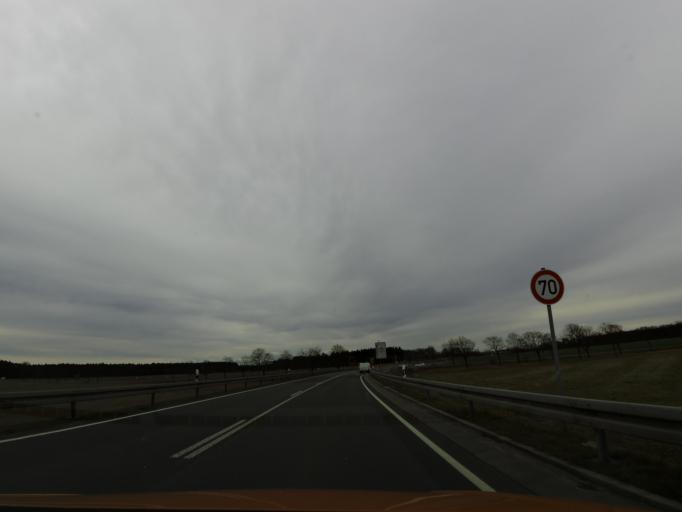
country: DE
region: Brandenburg
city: Belzig
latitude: 52.1479
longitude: 12.6183
